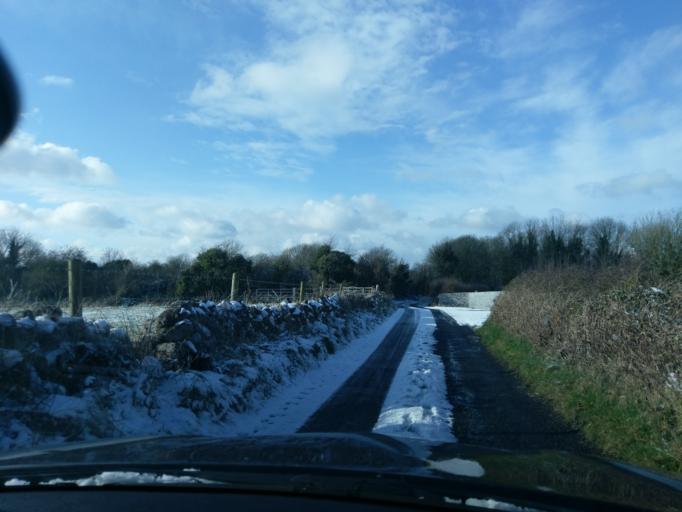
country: IE
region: Connaught
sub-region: County Galway
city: Athenry
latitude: 53.2102
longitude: -8.8166
